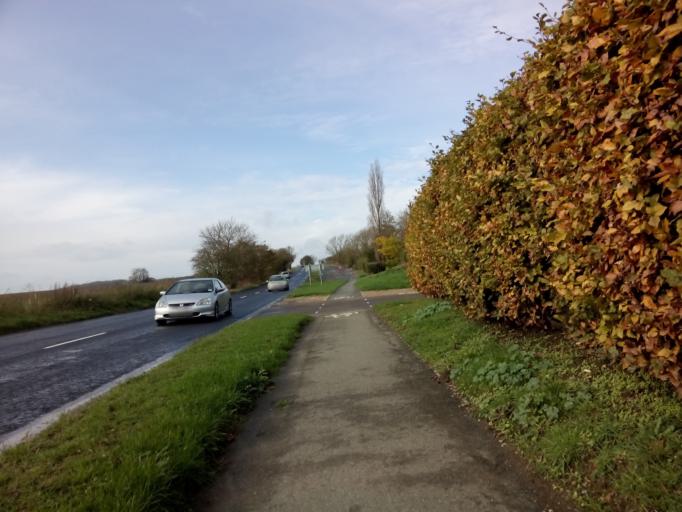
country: GB
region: England
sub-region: Suffolk
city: Needham Market
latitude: 52.1625
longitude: 1.0399
